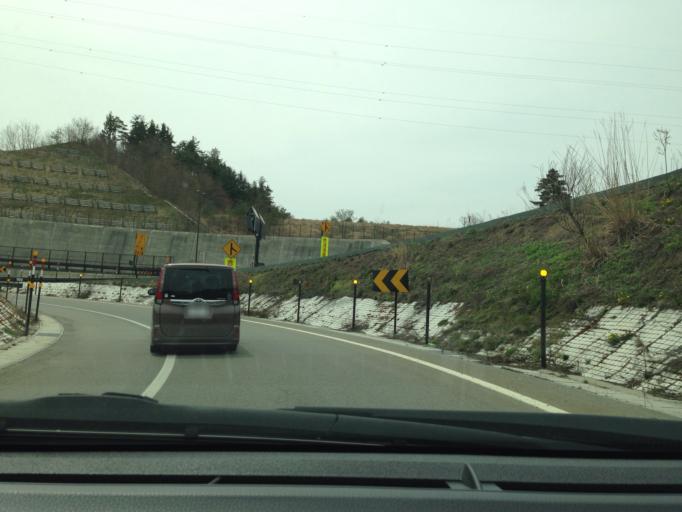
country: JP
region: Gifu
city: Takayama
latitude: 36.1683
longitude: 137.2271
